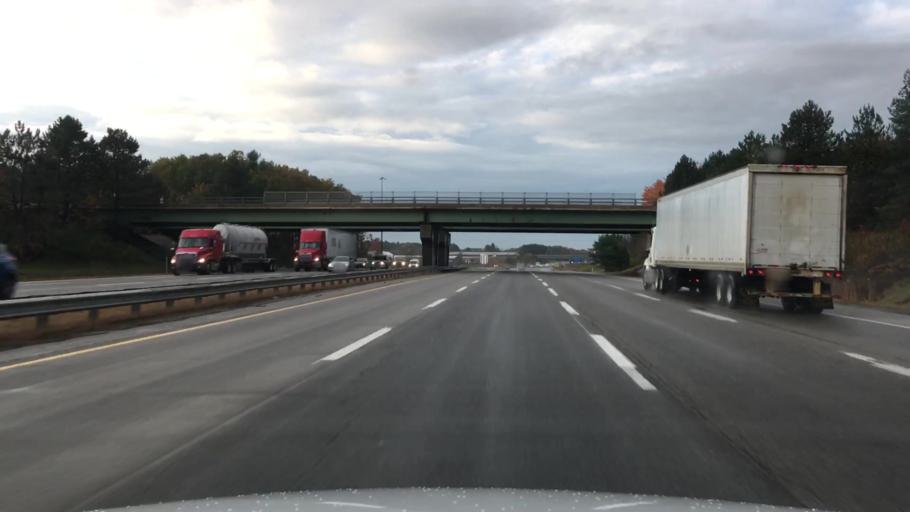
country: US
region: Maine
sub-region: York County
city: Saco
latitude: 43.5283
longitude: -70.4523
